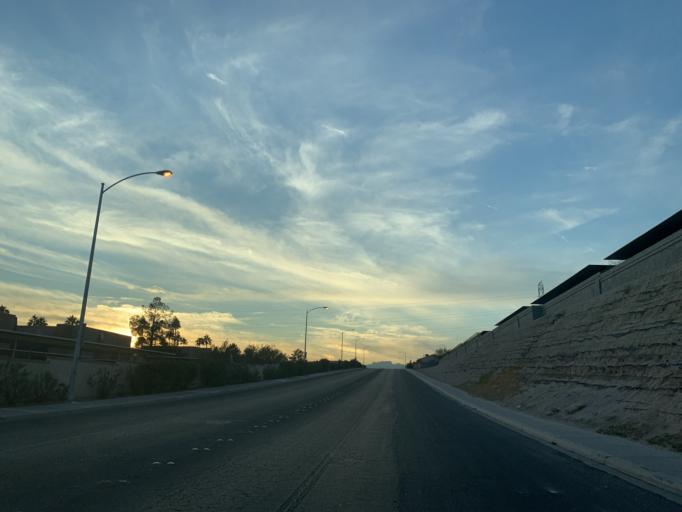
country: US
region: Nevada
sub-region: Clark County
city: Spring Valley
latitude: 36.1117
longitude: -115.2097
